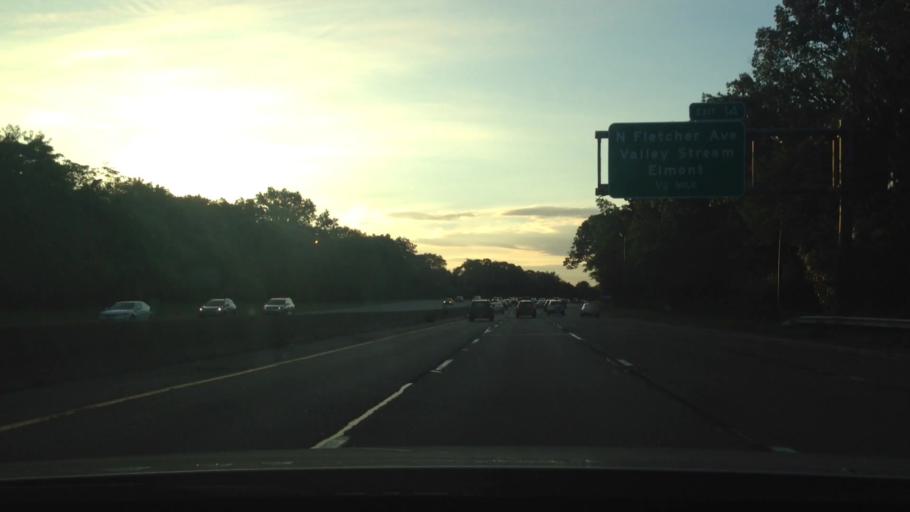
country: US
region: New York
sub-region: Nassau County
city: North Valley Stream
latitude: 40.6851
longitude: -73.7110
